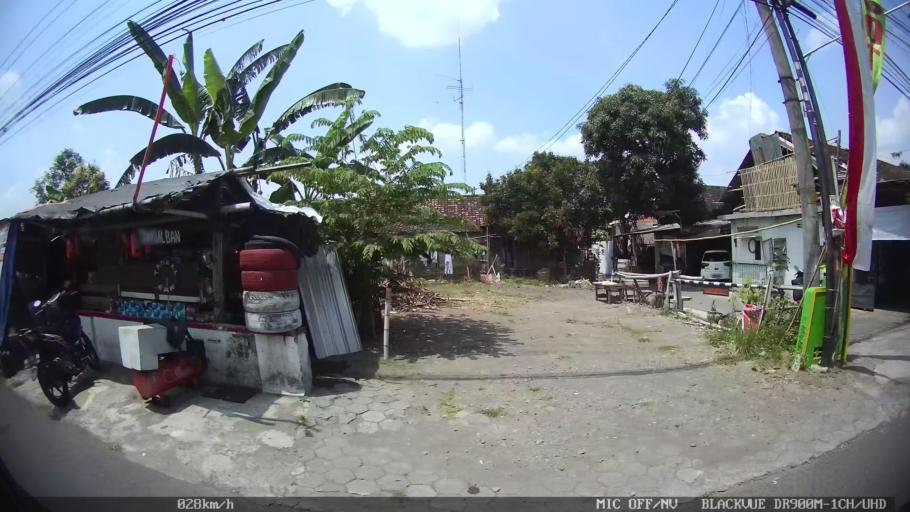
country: ID
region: Daerah Istimewa Yogyakarta
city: Yogyakarta
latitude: -7.8153
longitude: 110.4082
